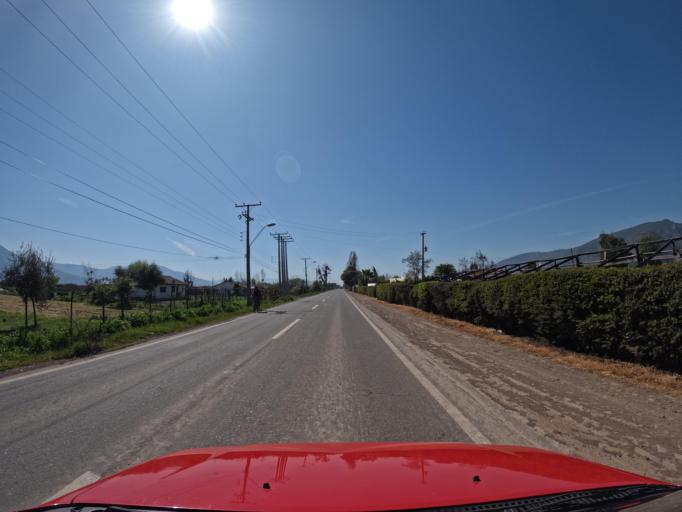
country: CL
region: Maule
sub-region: Provincia de Curico
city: Rauco
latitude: -35.0289
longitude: -71.4384
